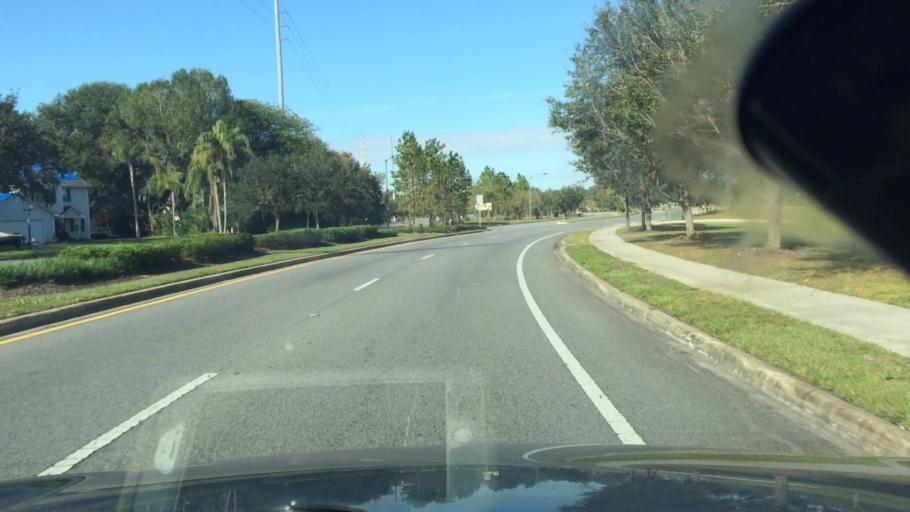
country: US
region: Florida
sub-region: Osceola County
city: Kissimmee
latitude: 28.2871
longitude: -81.3814
